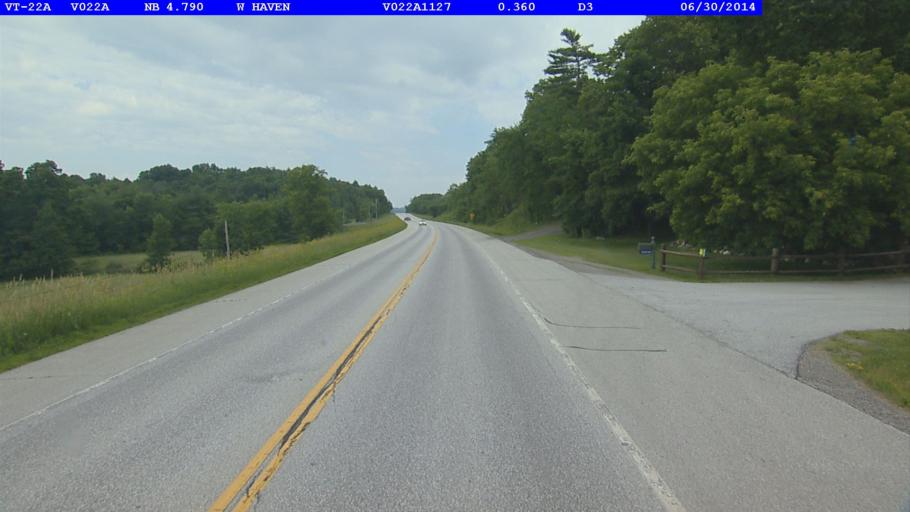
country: US
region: Vermont
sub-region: Rutland County
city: Fair Haven
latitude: 43.6335
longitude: -73.2968
